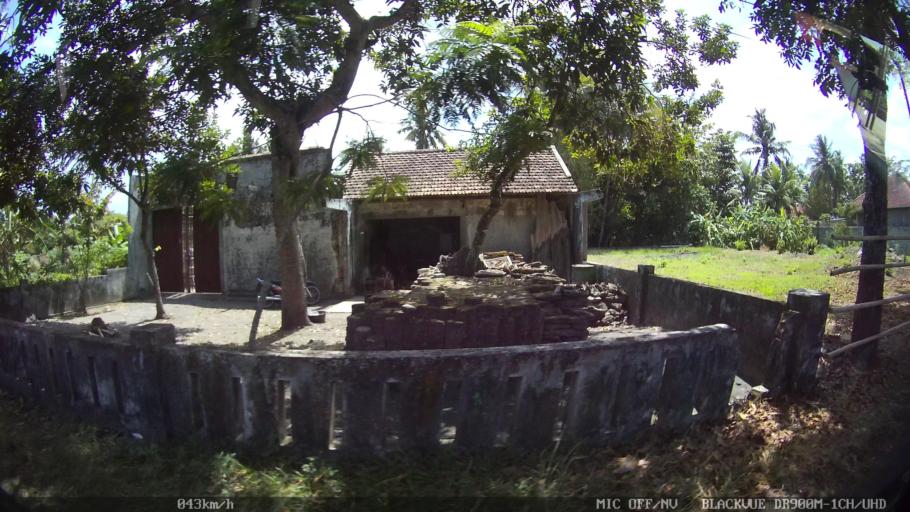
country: ID
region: Daerah Istimewa Yogyakarta
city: Bantul
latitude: -7.9049
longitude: 110.3246
